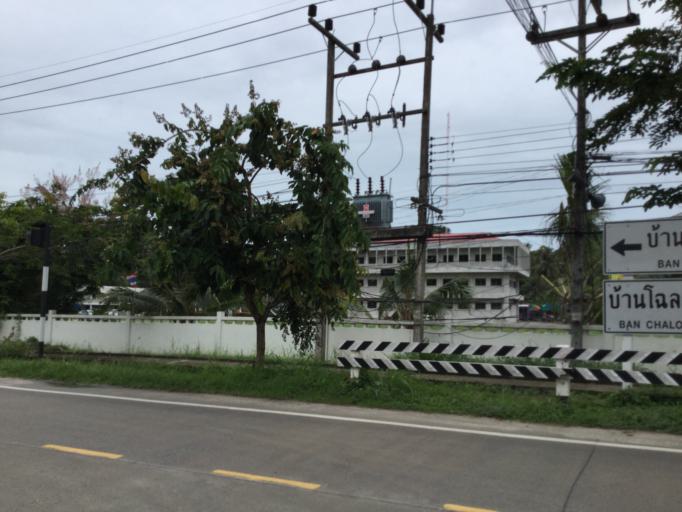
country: TH
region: Surat Thani
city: Ko Pha-Ngan
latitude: 9.7193
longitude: 99.9962
